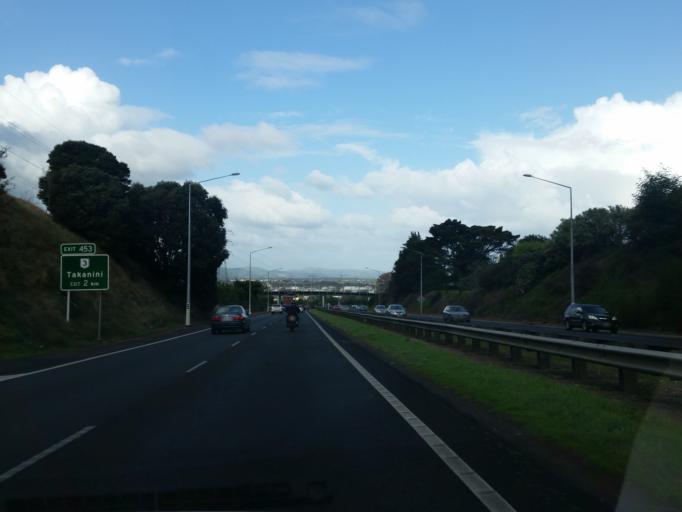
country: NZ
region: Auckland
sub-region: Auckland
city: Takanini
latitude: -37.0176
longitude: 174.9081
